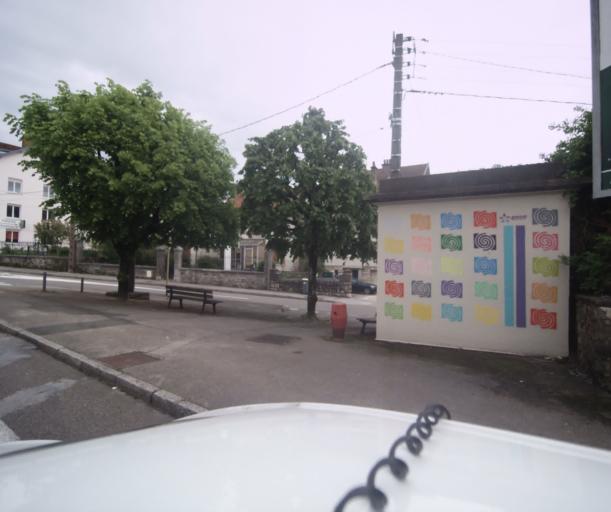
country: FR
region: Franche-Comte
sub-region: Departement du Doubs
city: Besancon
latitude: 47.2546
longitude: 6.0392
